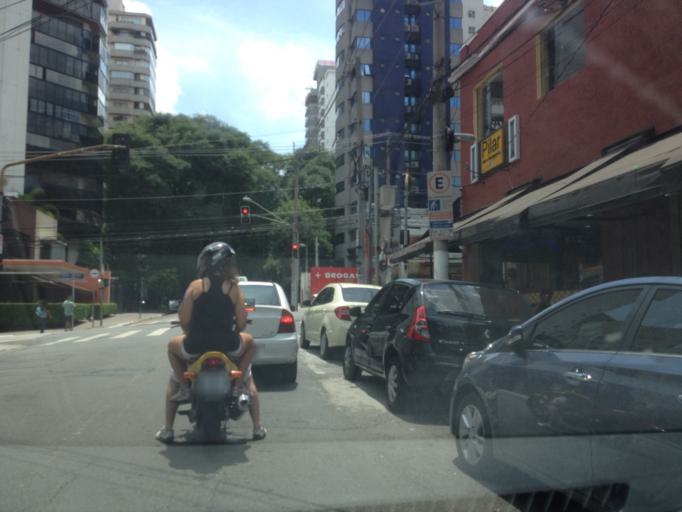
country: BR
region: Sao Paulo
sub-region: Sao Paulo
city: Sao Paulo
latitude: -23.5706
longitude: -46.6570
